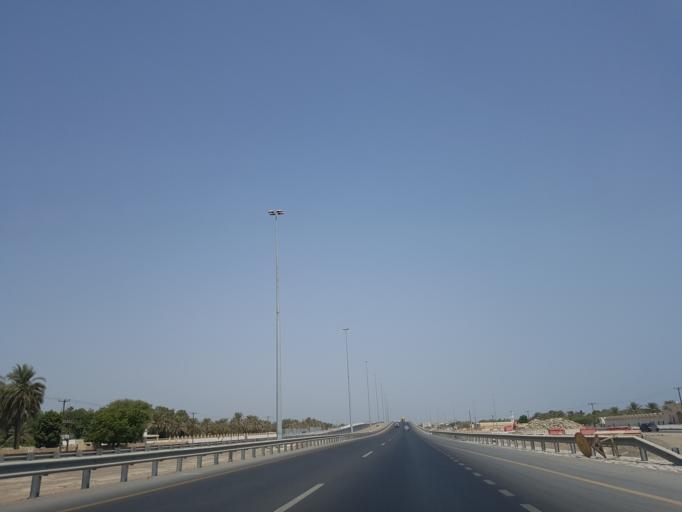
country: OM
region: Al Batinah
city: Saham
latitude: 24.1004
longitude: 56.9216
